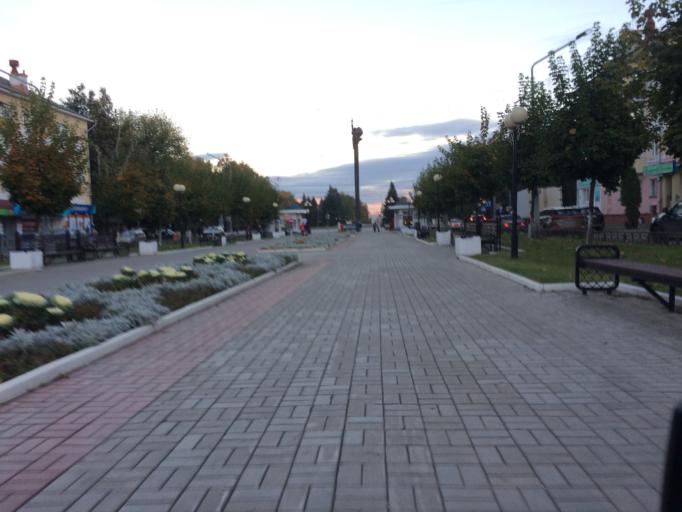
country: RU
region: Mariy-El
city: Yoshkar-Ola
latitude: 56.6376
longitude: 47.8848
